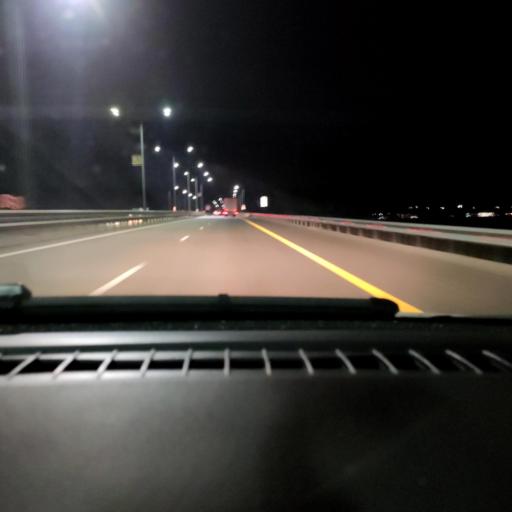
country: RU
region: Voronezj
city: Kashirskoye
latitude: 51.4835
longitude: 39.5406
